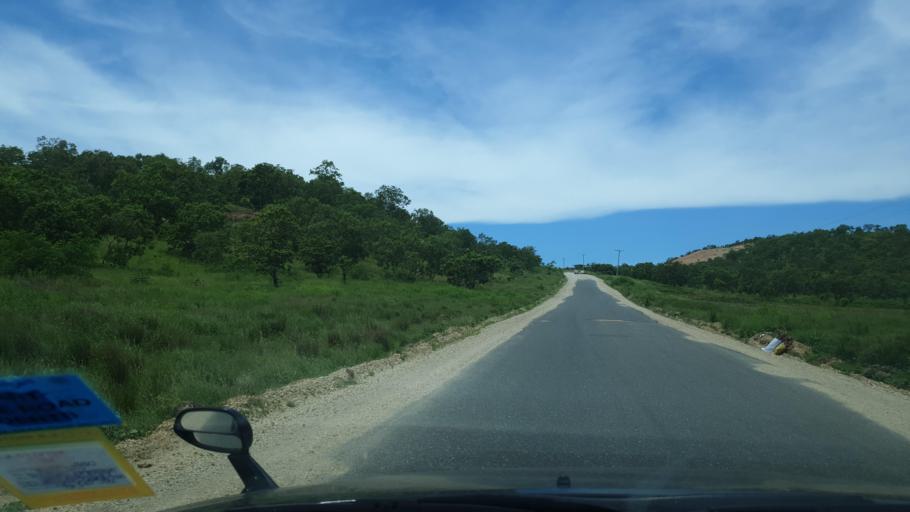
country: PG
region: National Capital
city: Port Moresby
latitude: -9.4332
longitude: 147.0742
